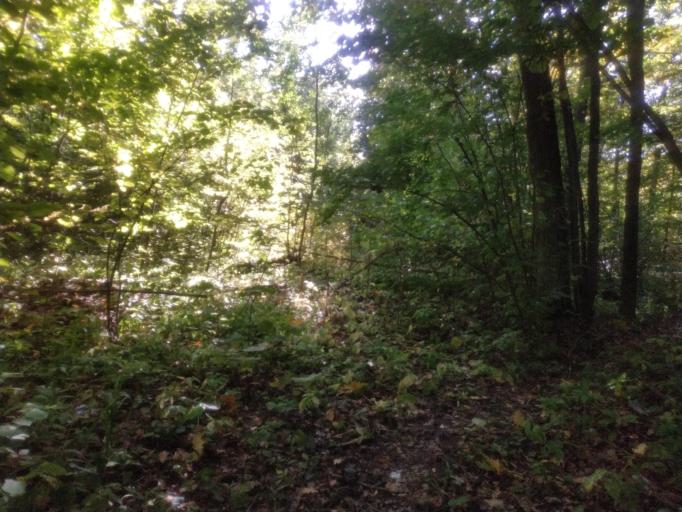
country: RU
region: Chuvashia
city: Novyye Lapsary
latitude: 56.1381
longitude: 47.1371
